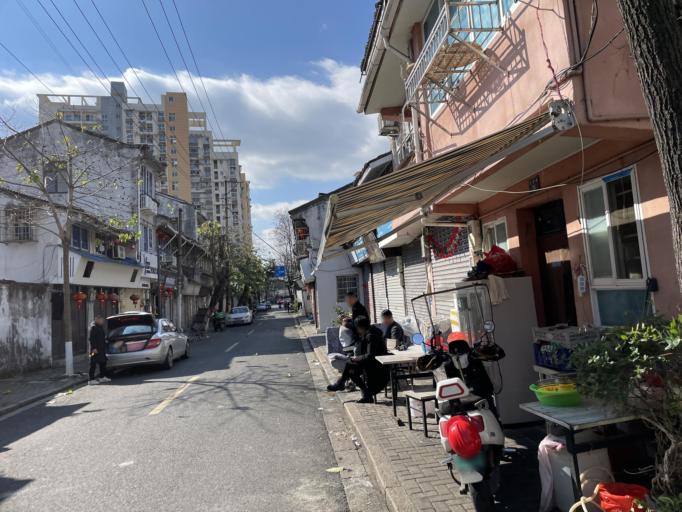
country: CN
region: Zhejiang Sheng
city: Wuma
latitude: 28.0206
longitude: 120.6485
